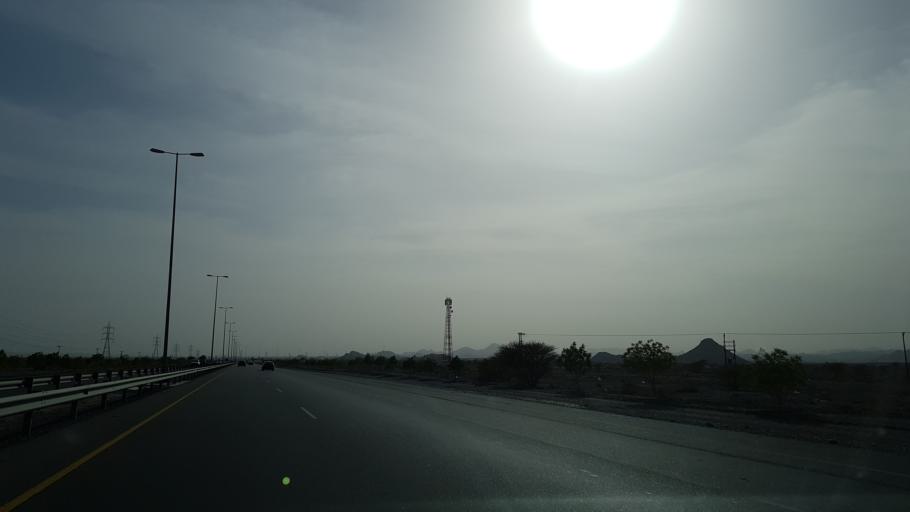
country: OM
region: Muhafazat ad Dakhiliyah
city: Nizwa
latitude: 22.8657
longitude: 57.5994
